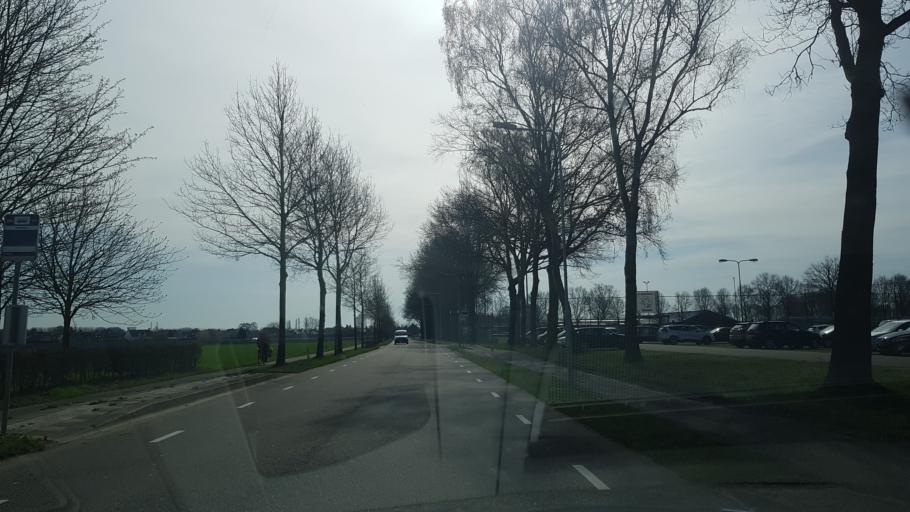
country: NL
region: Limburg
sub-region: Gemeente Leudal
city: Kelpen-Oler
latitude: 51.1690
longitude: 5.8277
